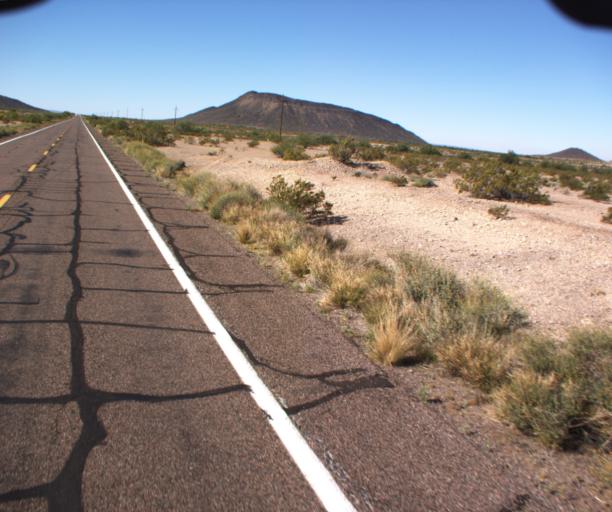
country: US
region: Arizona
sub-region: Maricopa County
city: Gila Bend
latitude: 32.7836
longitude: -112.8088
